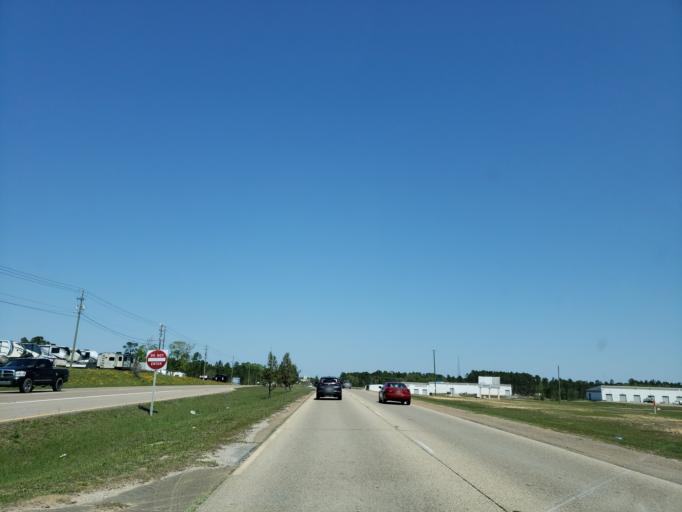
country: US
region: Mississippi
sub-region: Harrison County
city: Lyman
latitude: 30.4873
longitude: -89.1042
